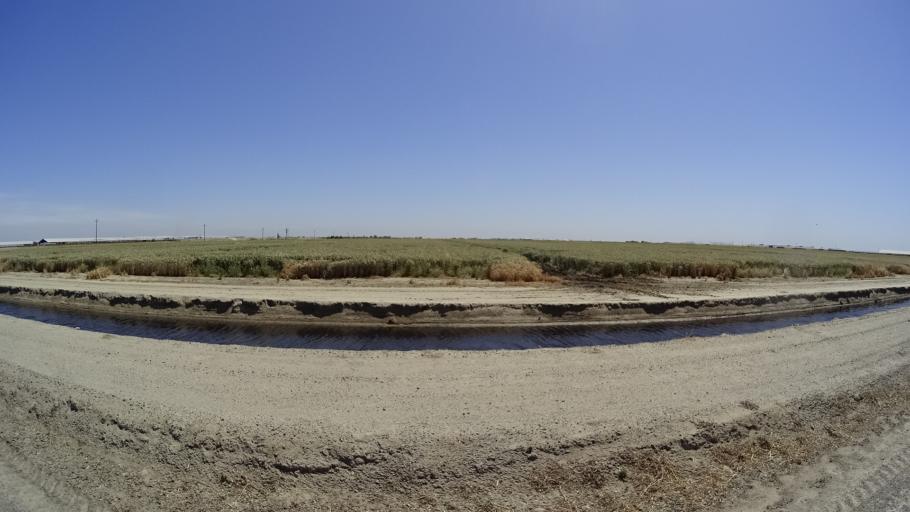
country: US
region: California
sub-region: Kings County
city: Home Garden
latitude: 36.1952
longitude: -119.6906
